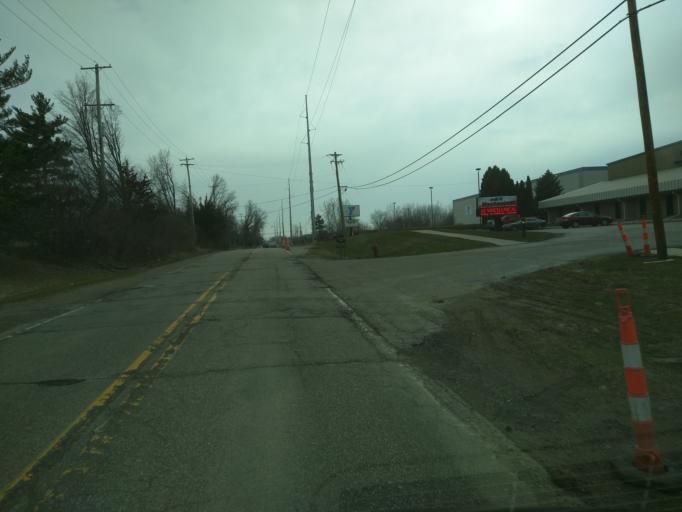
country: US
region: Michigan
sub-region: Ingham County
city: Edgemont Park
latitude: 42.7179
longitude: -84.5974
